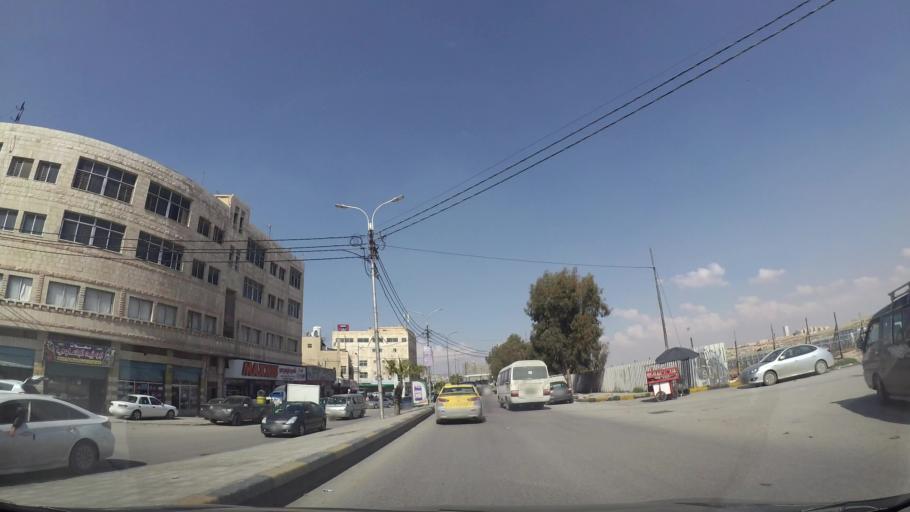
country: JO
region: Zarqa
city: Zarqa
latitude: 32.0686
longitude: 36.0971
